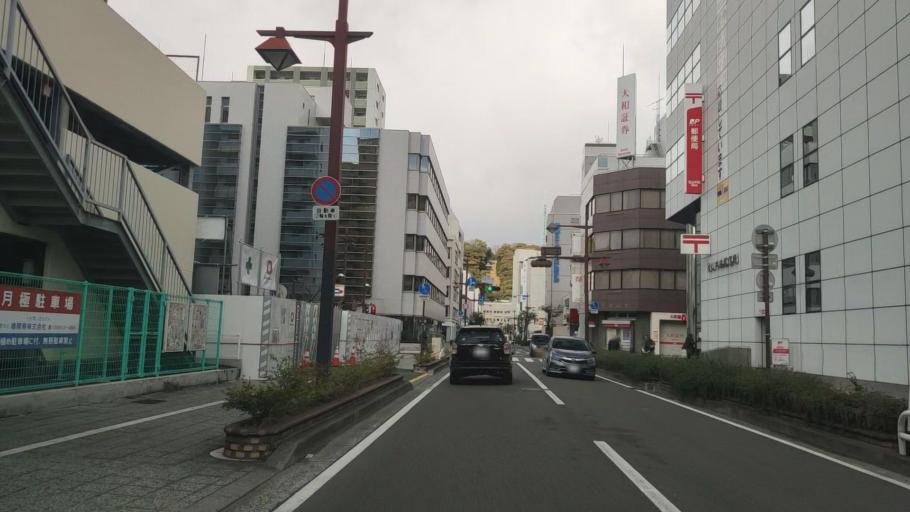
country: JP
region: Ehime
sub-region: Shikoku-chuo Shi
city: Matsuyama
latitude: 33.8379
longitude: 132.7680
